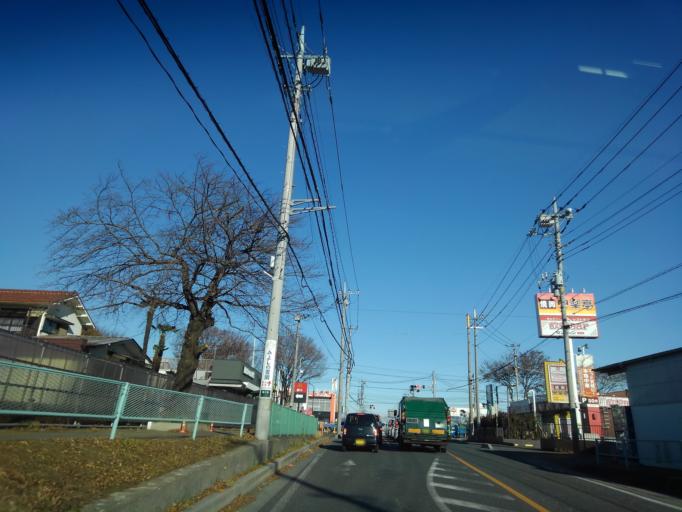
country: JP
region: Saitama
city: Oi
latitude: 35.8084
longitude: 139.5215
